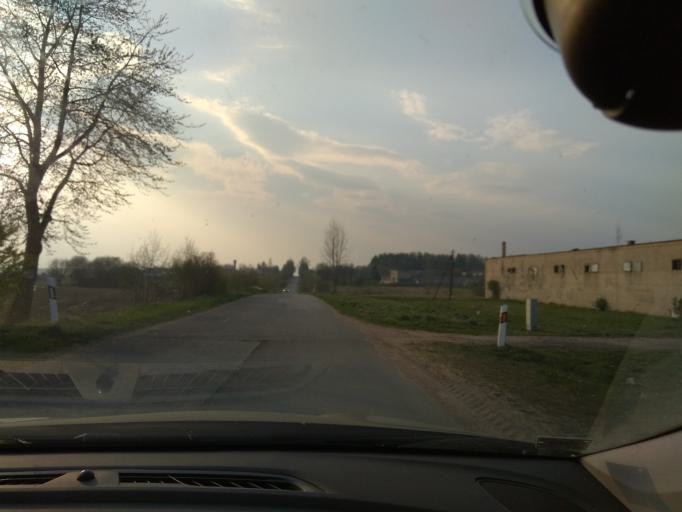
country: LT
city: Baltoji Voke
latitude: 54.5948
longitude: 25.1519
